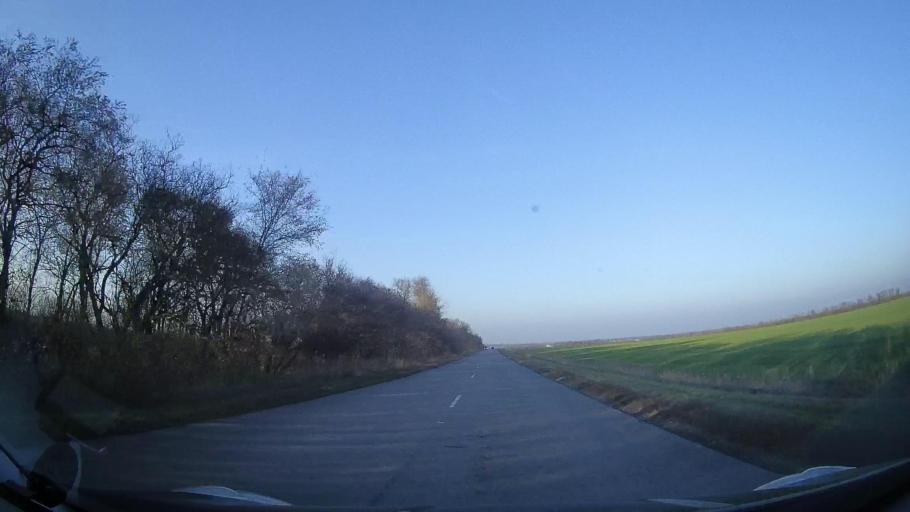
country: RU
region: Rostov
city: Kirovskaya
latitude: 47.0155
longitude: 39.9789
